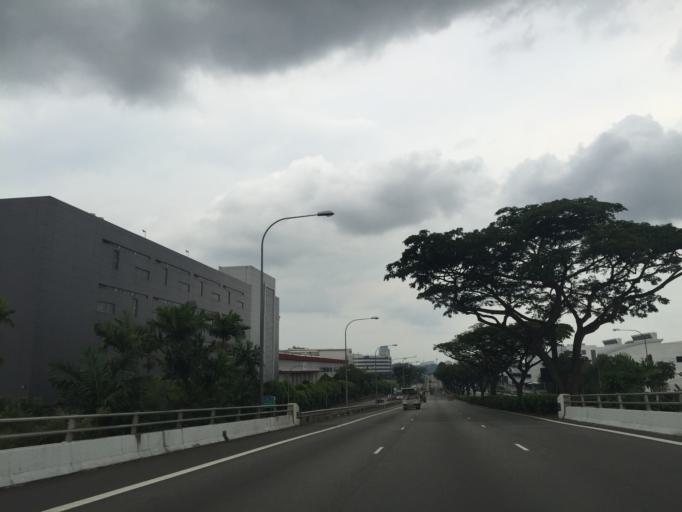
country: SG
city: Singapore
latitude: 1.3221
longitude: 103.7128
